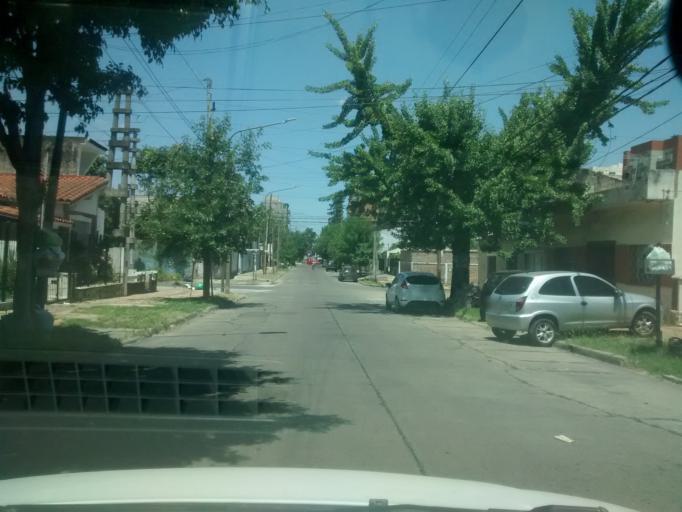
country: AR
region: Buenos Aires
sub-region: Partido de Moron
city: Moron
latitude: -34.6567
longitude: -58.6164
